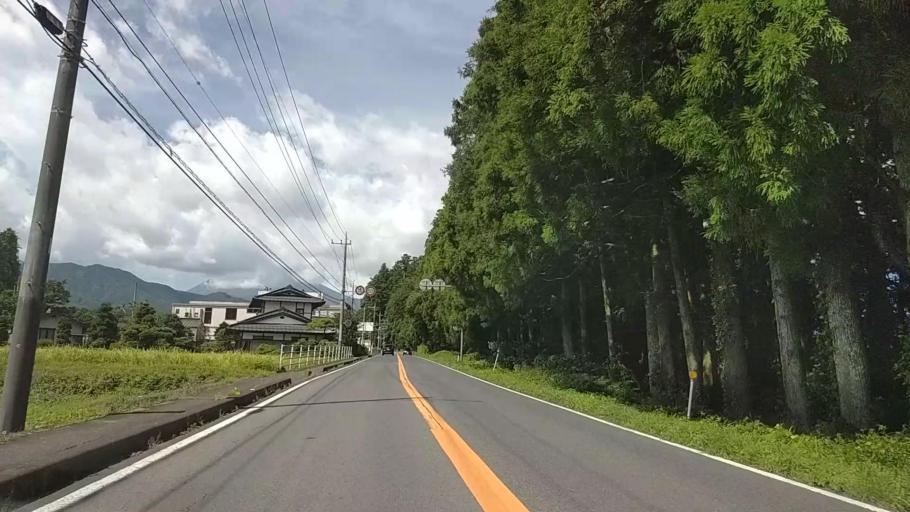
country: JP
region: Tochigi
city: Imaichi
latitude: 36.7316
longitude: 139.6637
